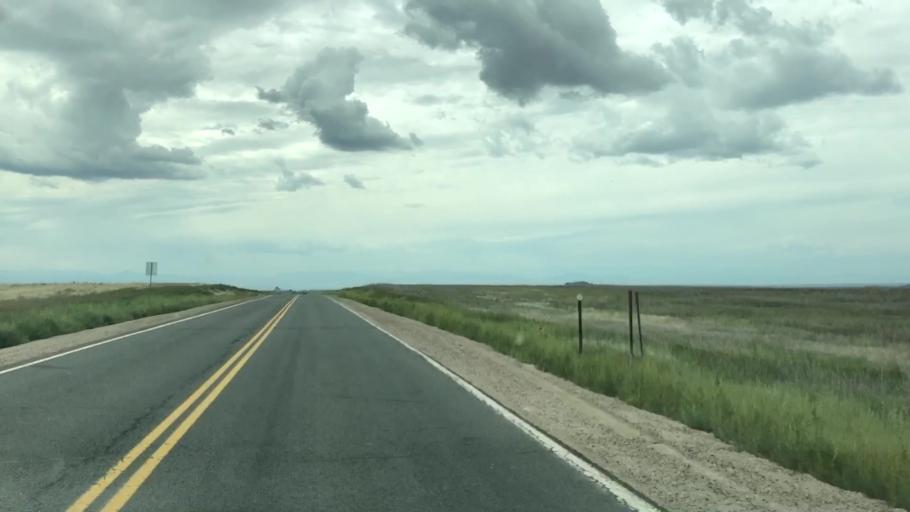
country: US
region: Colorado
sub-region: Adams County
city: Aurora
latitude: 39.7984
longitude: -104.6807
